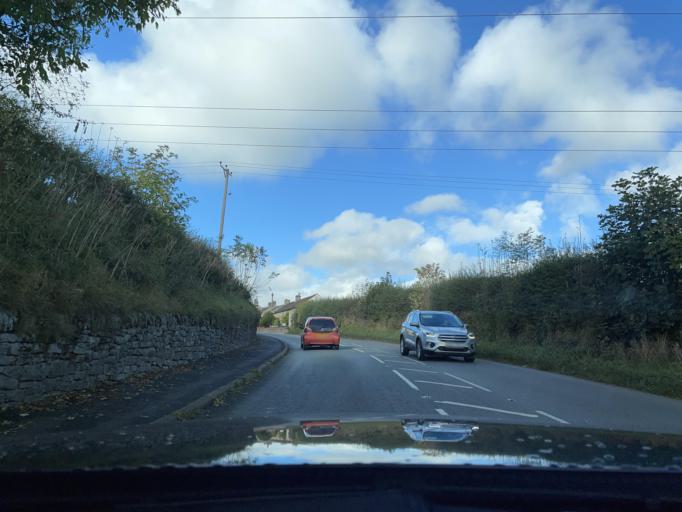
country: GB
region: England
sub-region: Derbyshire
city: Hope Valley
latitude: 53.3469
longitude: -1.7384
